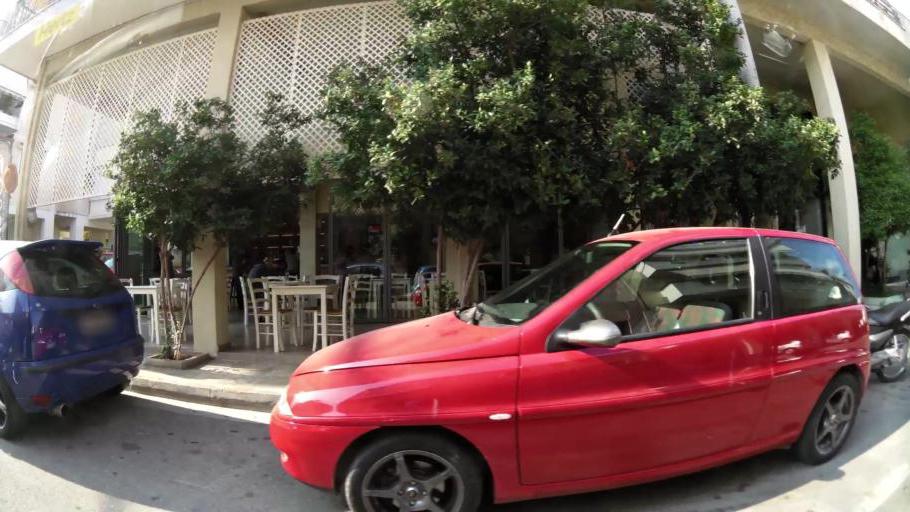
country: GR
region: Attica
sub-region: Nomarchia Athinas
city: Petroupolis
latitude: 38.0475
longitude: 23.6943
